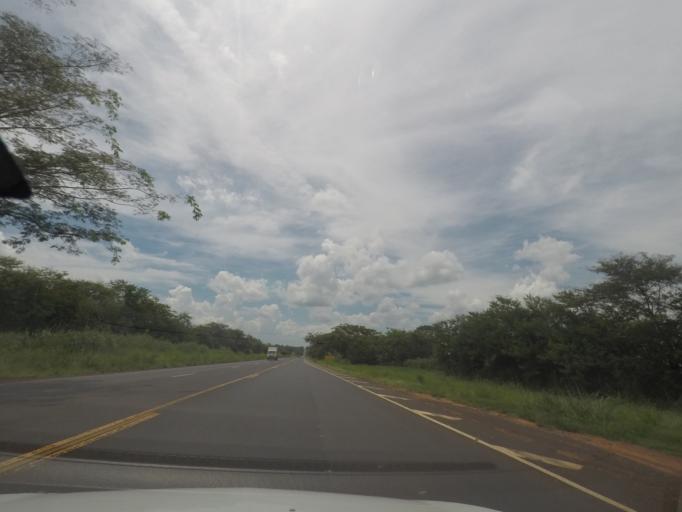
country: BR
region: Sao Paulo
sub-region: Barretos
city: Barretos
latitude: -20.4174
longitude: -48.6317
